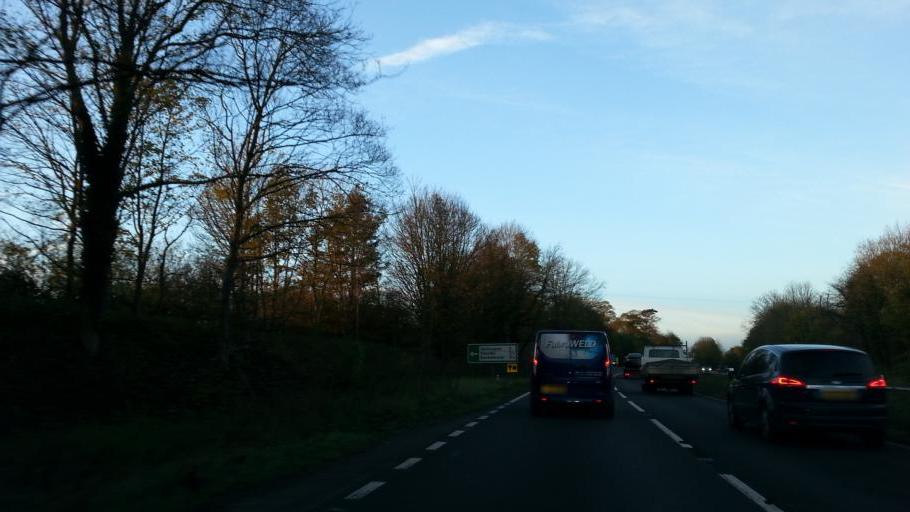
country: GB
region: England
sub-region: Lincolnshire
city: Grantham
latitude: 52.8264
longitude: -0.6304
